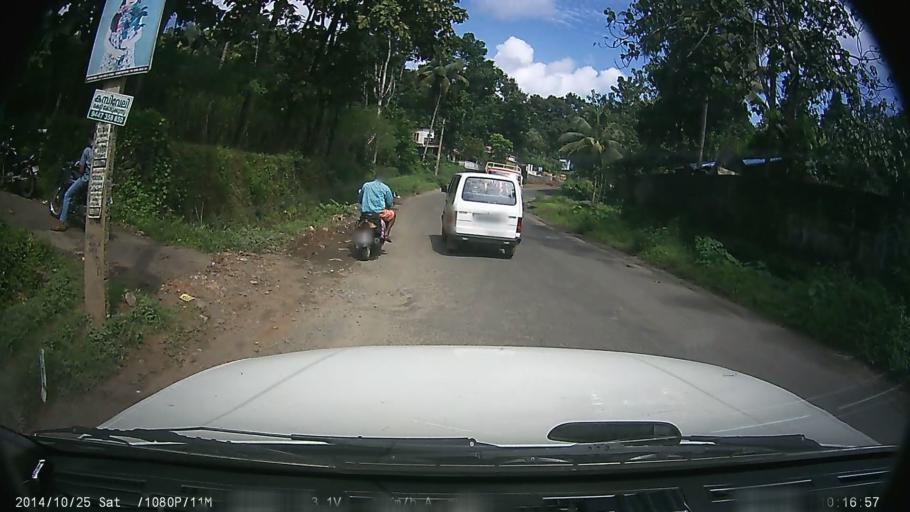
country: IN
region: Kerala
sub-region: Ernakulam
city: Piravam
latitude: 9.8785
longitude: 76.5955
